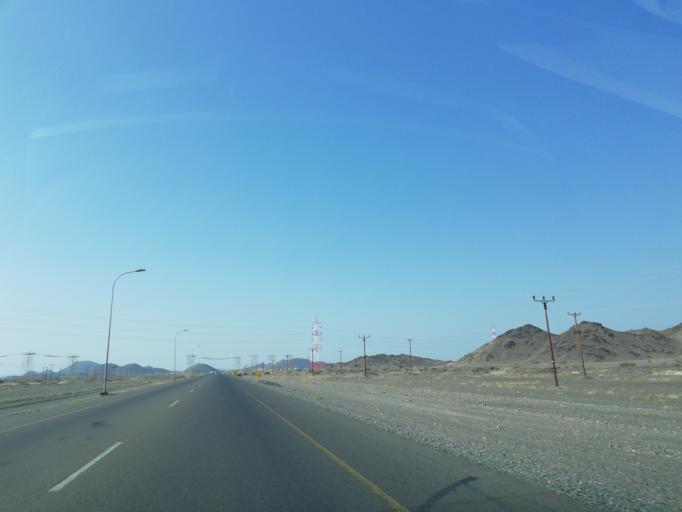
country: OM
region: Ash Sharqiyah
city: Ibra'
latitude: 22.7492
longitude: 58.1483
